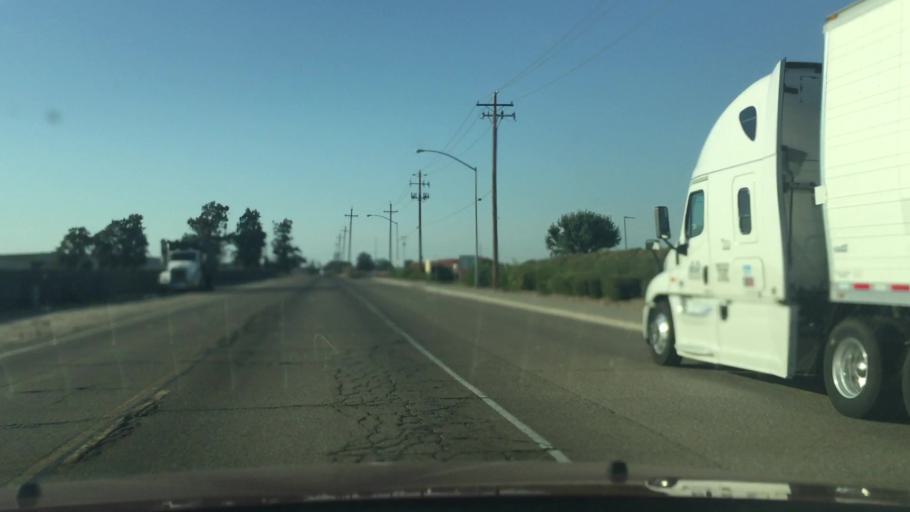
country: US
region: California
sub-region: San Joaquin County
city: Lathrop
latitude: 37.8068
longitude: -121.2711
